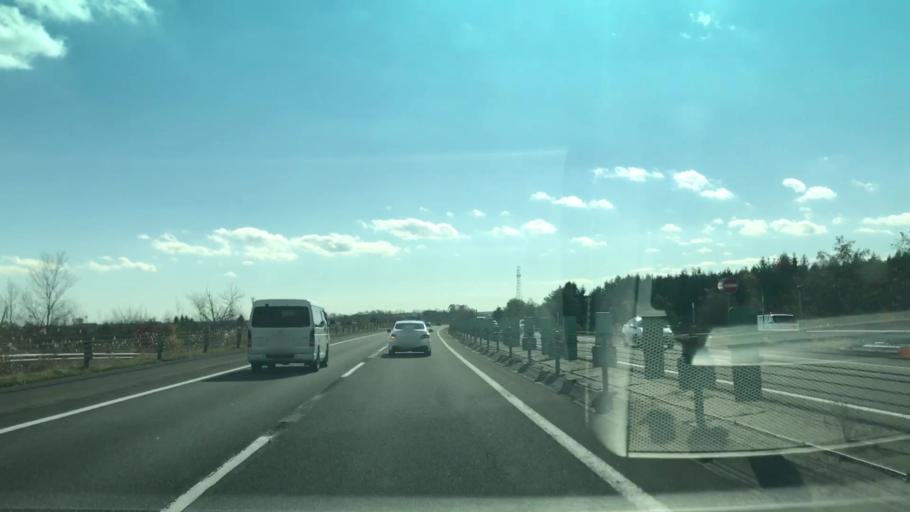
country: JP
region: Hokkaido
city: Kitahiroshima
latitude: 42.9056
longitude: 141.5507
